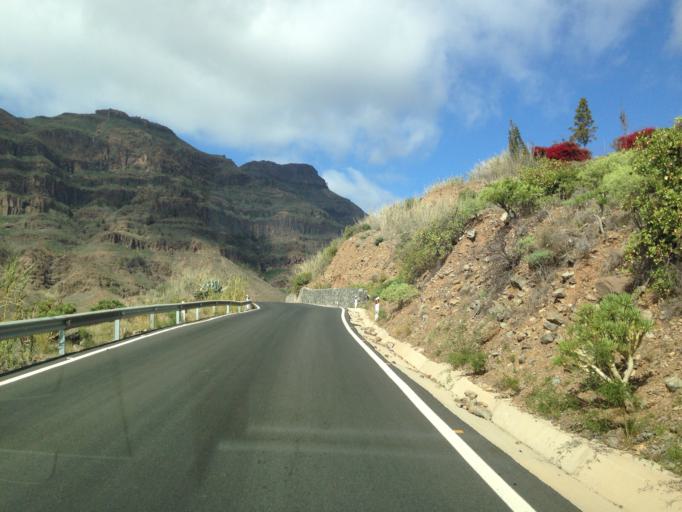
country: ES
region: Canary Islands
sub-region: Provincia de Las Palmas
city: Santa Lucia
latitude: 27.8732
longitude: -15.5648
